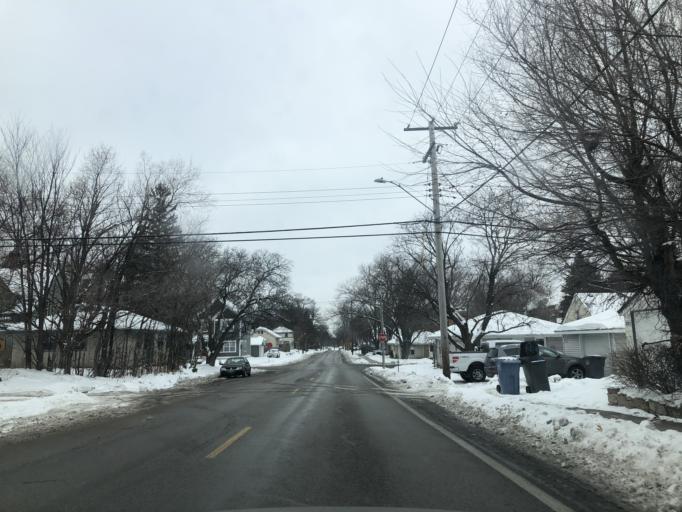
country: US
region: Minnesota
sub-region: Hennepin County
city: Robbinsdale
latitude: 45.0241
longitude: -93.3125
